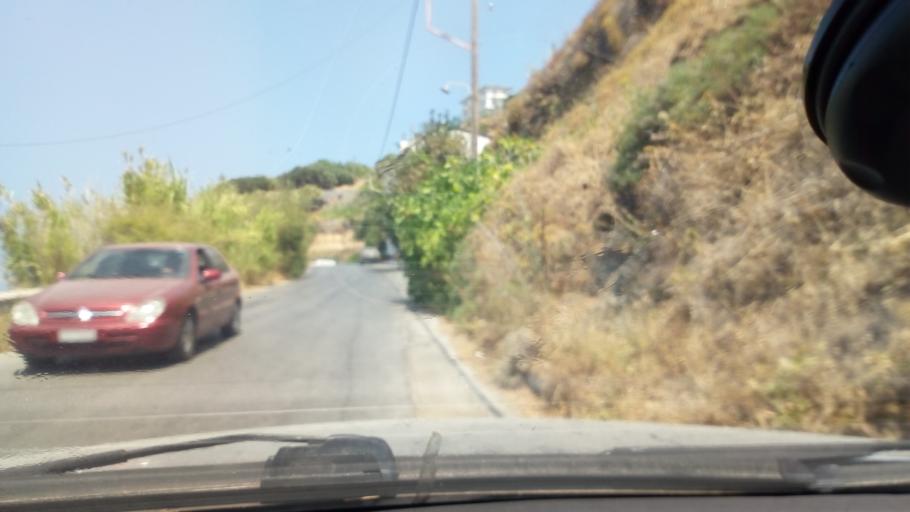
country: GR
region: North Aegean
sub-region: Nomos Samou
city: Agios Kirykos
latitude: 37.6298
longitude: 26.1700
